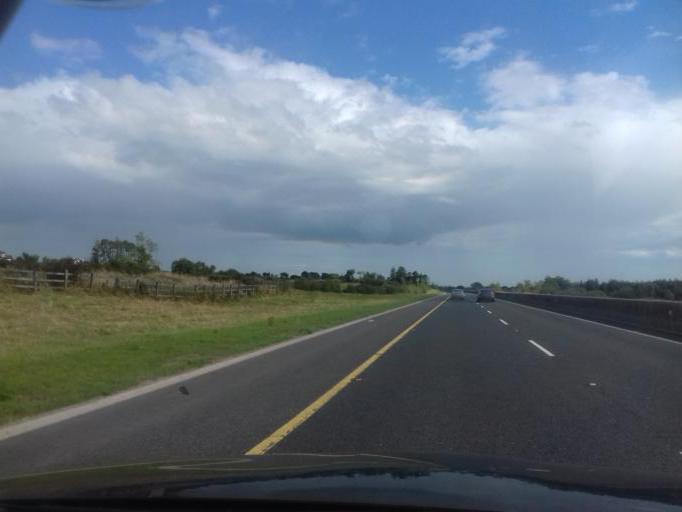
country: IE
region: Leinster
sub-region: Kilkenny
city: Mooncoin
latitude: 52.4204
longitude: -7.2236
